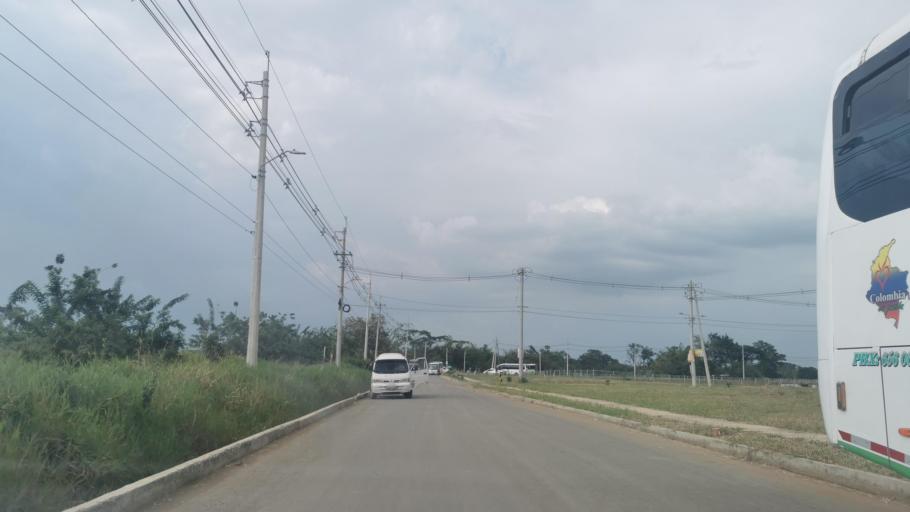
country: CO
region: Valle del Cauca
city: Jamundi
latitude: 3.2366
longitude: -76.5270
